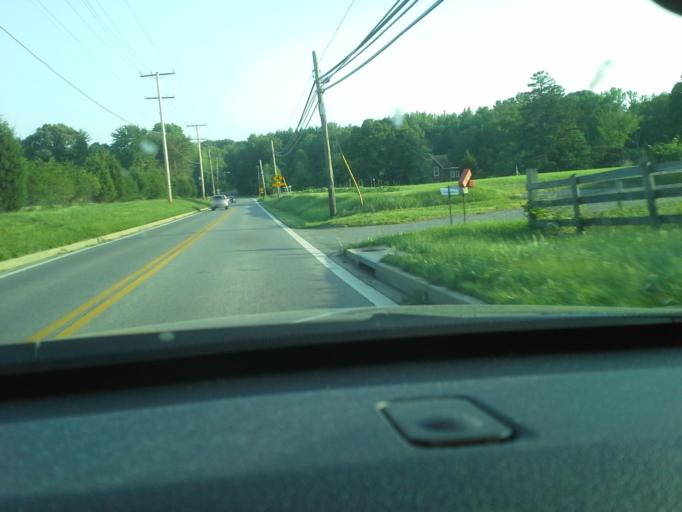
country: US
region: Maryland
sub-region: Anne Arundel County
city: Shady Side
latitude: 38.8423
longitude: -76.5605
